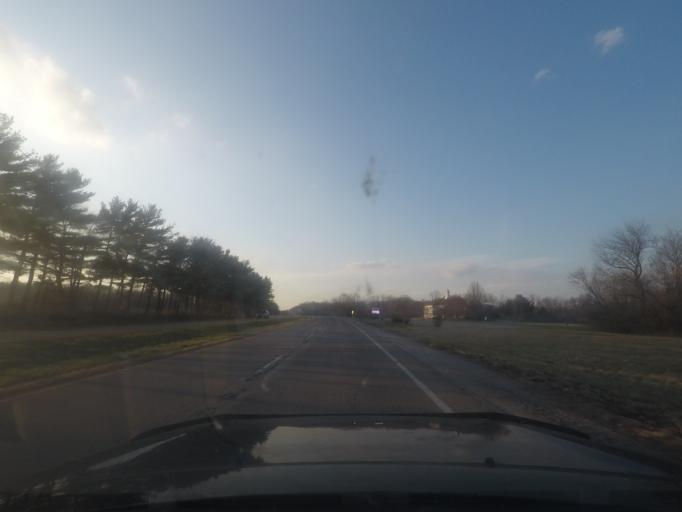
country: US
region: Indiana
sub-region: LaPorte County
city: LaPorte
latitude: 41.5864
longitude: -86.7010
